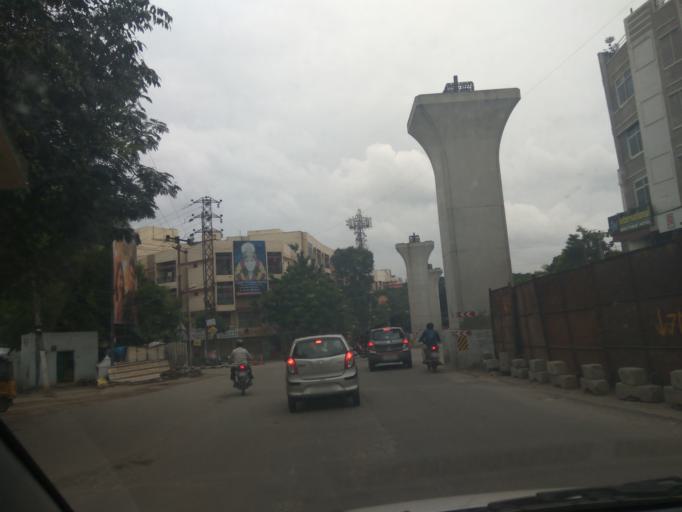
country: IN
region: Telangana
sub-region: Hyderabad
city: Malkajgiri
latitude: 17.4306
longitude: 78.5051
